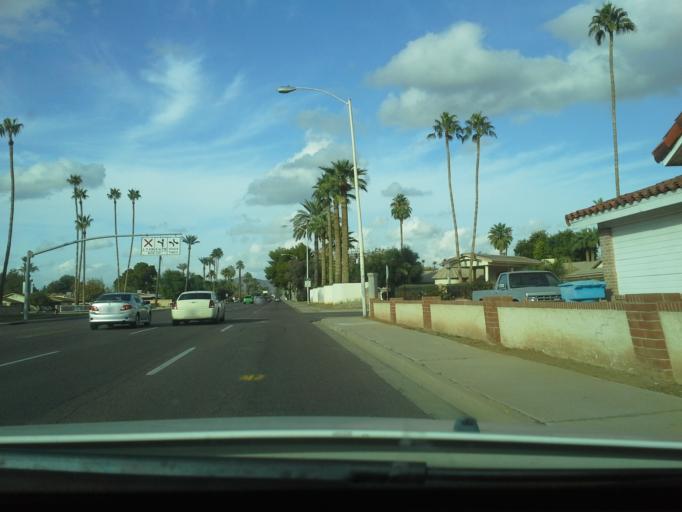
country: US
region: Arizona
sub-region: Maricopa County
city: Phoenix
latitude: 33.5253
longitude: -112.0823
